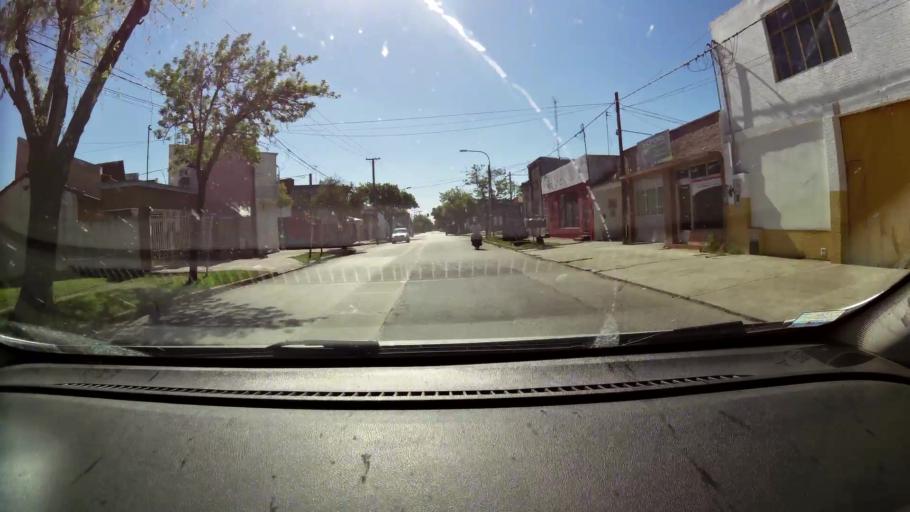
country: AR
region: Santa Fe
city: Rafaela
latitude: -31.2448
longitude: -61.4812
